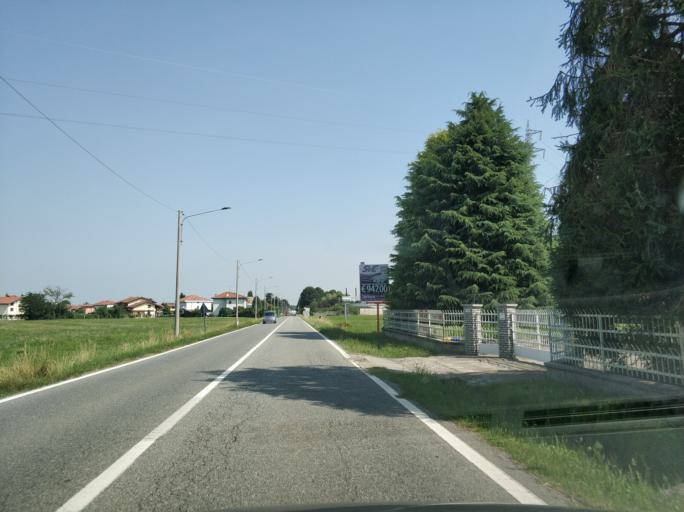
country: IT
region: Piedmont
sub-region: Provincia di Torino
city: Oglianico
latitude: 45.3474
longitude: 7.7049
